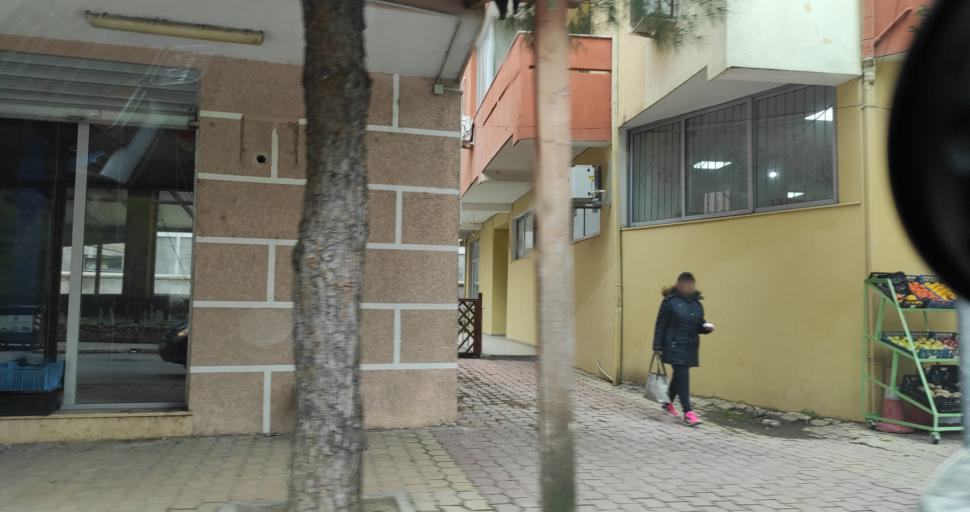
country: AL
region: Lezhe
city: Shengjin
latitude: 41.8095
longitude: 19.5993
